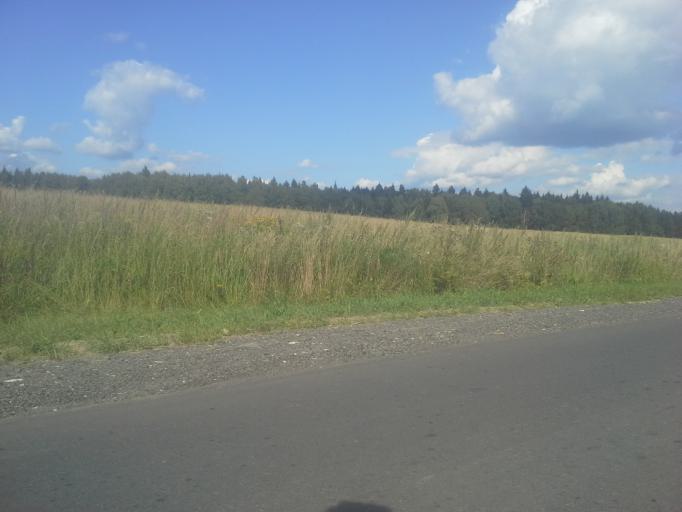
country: RU
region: Moskovskaya
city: Kievskij
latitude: 55.3153
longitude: 37.0281
